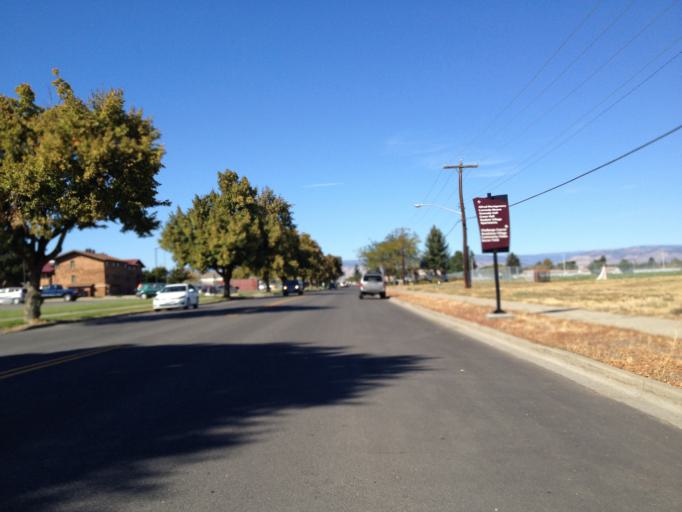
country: US
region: Washington
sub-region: Kittitas County
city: Ellensburg
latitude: 47.0078
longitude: -120.5319
